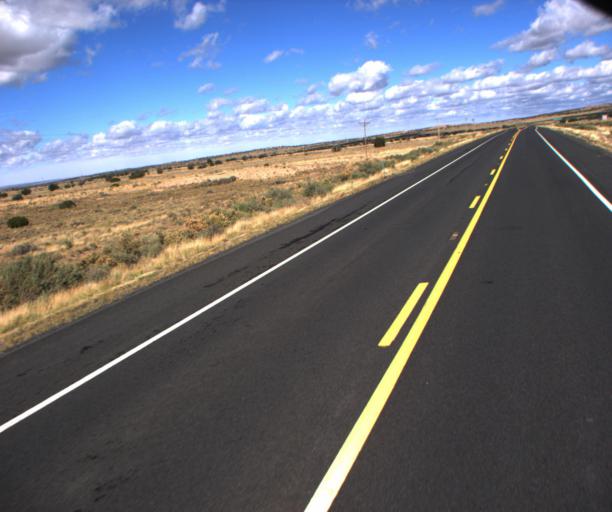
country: US
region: Arizona
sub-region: Apache County
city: Houck
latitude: 35.0437
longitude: -109.2705
